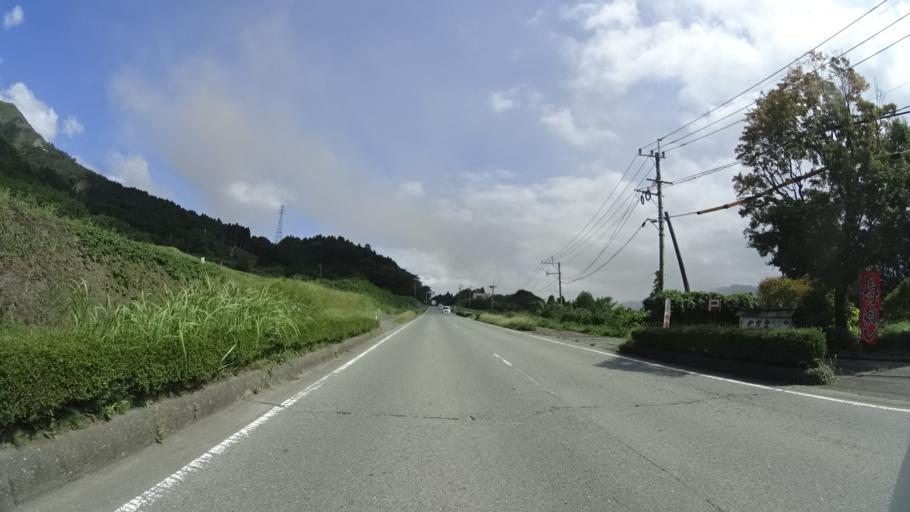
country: JP
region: Kumamoto
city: Aso
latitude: 32.8462
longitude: 131.0349
